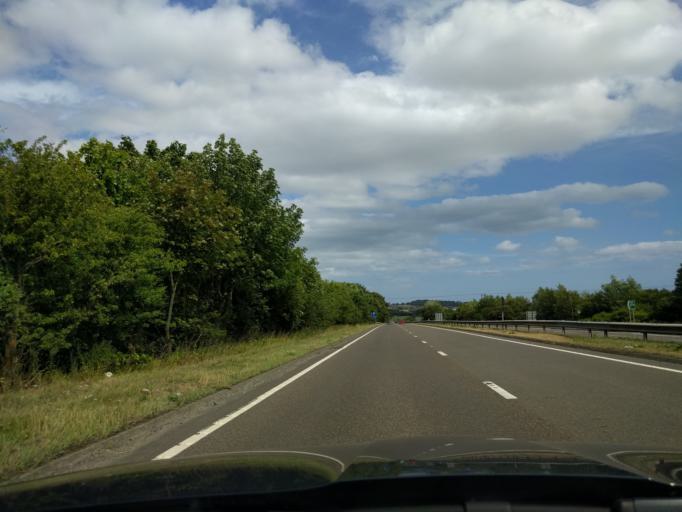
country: GB
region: England
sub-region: Northumberland
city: Alnwick
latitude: 55.4002
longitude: -1.6919
